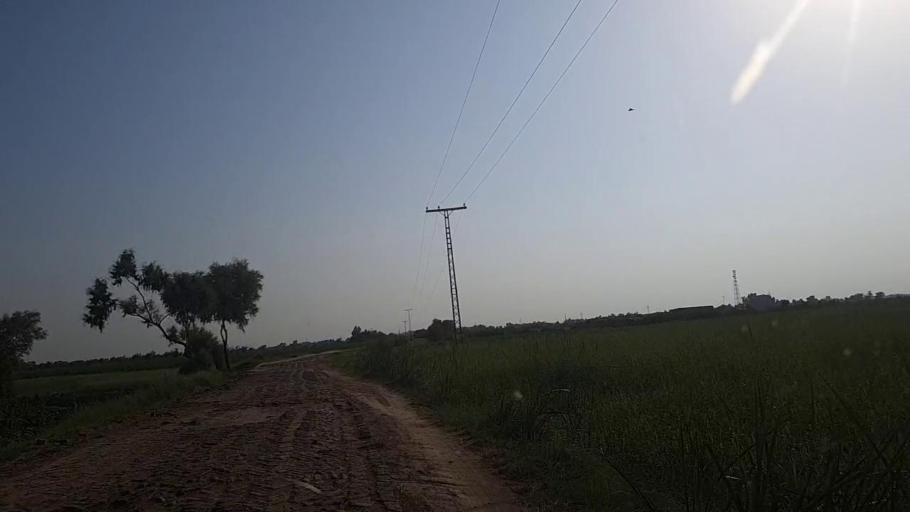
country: PK
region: Sindh
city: Khanpur
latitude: 27.7290
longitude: 69.3121
